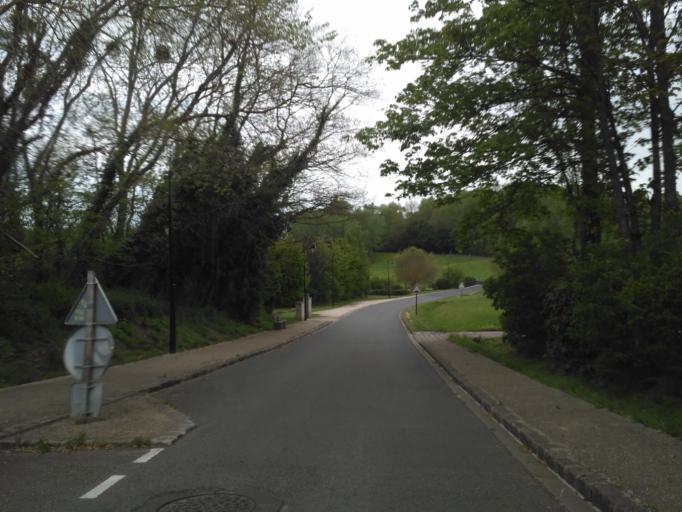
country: FR
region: Ile-de-France
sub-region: Departement de Seine-et-Marne
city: Moisenay
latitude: 48.5699
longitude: 2.7816
